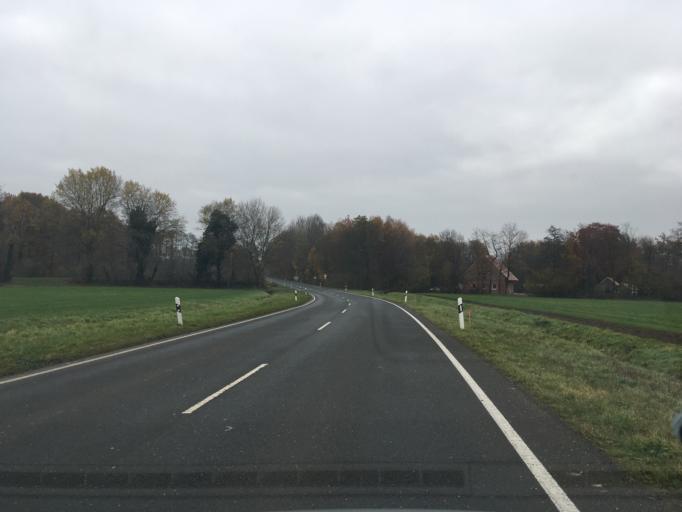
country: DE
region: North Rhine-Westphalia
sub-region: Regierungsbezirk Munster
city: Legden
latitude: 52.0205
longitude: 7.0554
